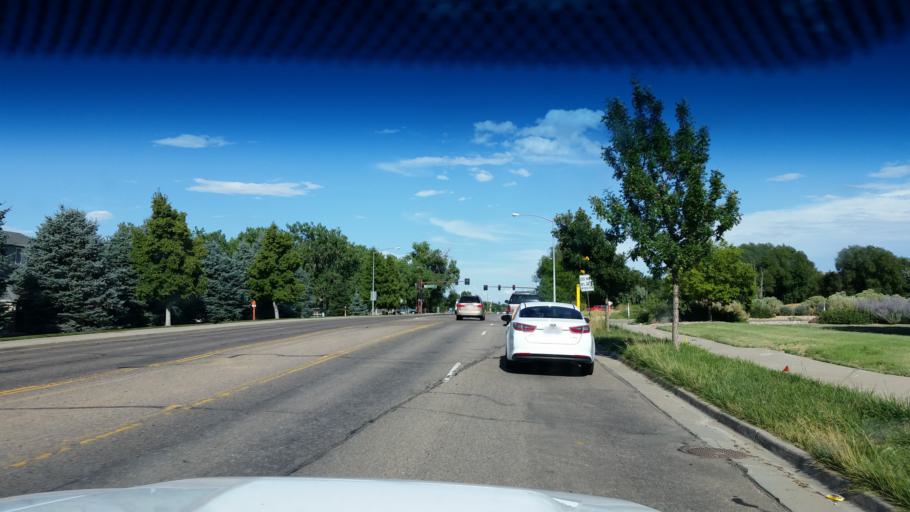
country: US
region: Colorado
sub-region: Adams County
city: Northglenn
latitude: 39.9284
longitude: -104.9708
